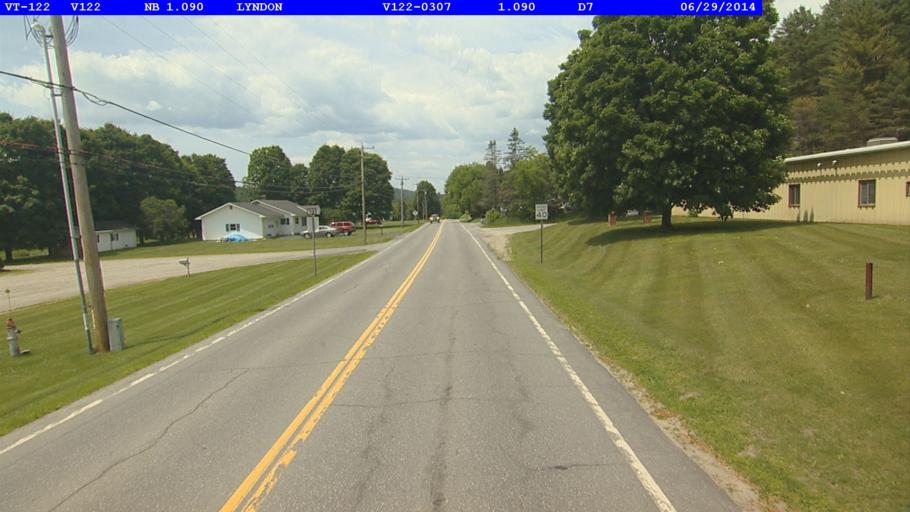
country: US
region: Vermont
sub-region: Caledonia County
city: Lyndonville
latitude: 44.5468
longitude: -72.0190
